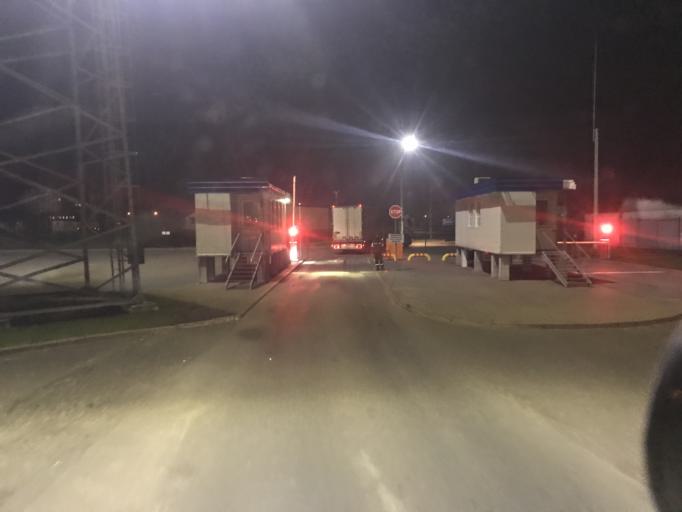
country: PL
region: Lublin Voivodeship
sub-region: Powiat bialski
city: Terespol
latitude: 52.1236
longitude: 23.5775
